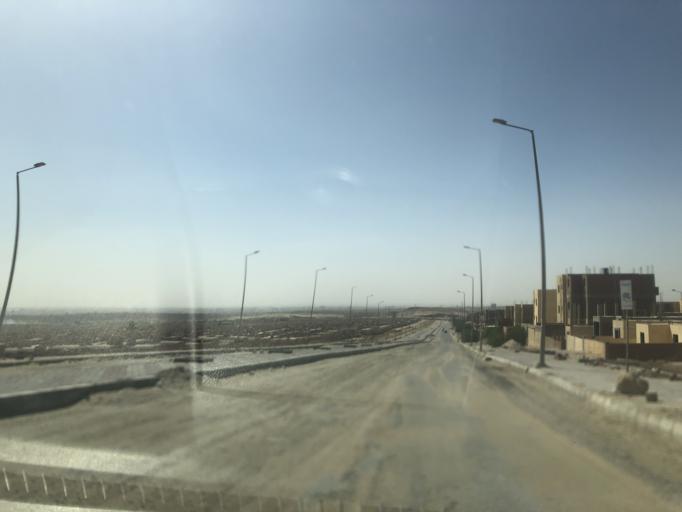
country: EG
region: Al Jizah
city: Madinat Sittah Uktubar
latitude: 29.9299
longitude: 30.9683
